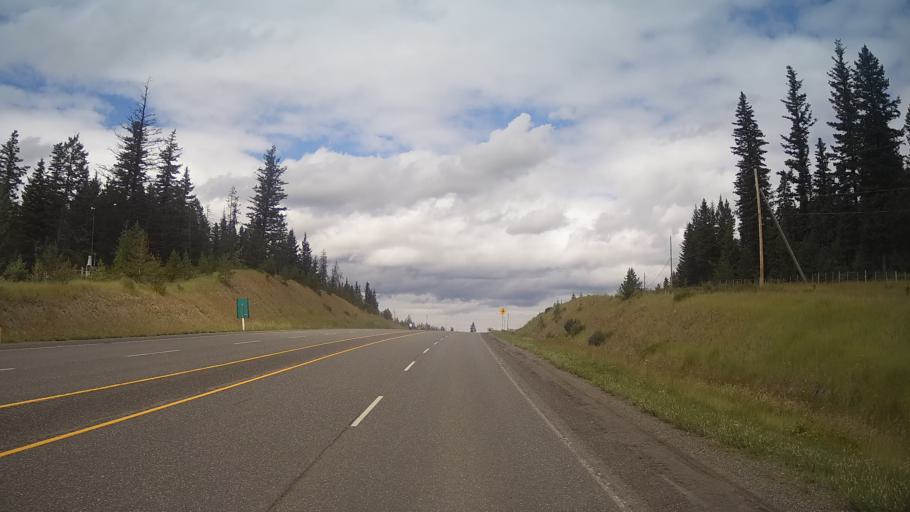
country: CA
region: British Columbia
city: Cache Creek
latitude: 51.4754
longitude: -121.3704
